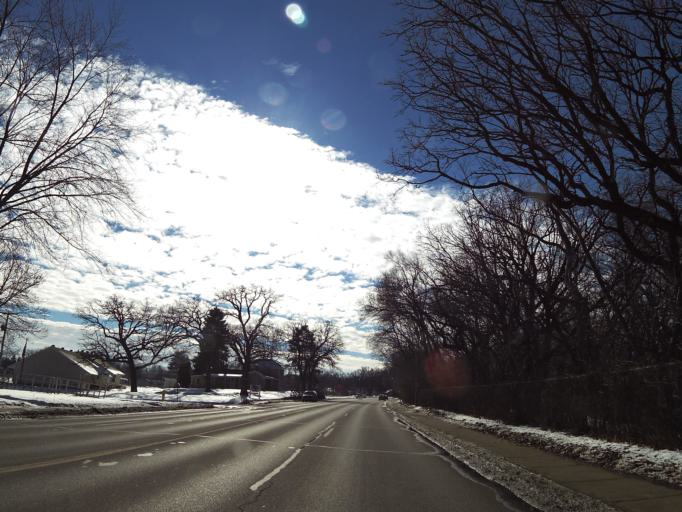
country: US
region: Minnesota
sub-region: Hennepin County
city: Richfield
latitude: 44.8786
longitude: -93.2883
